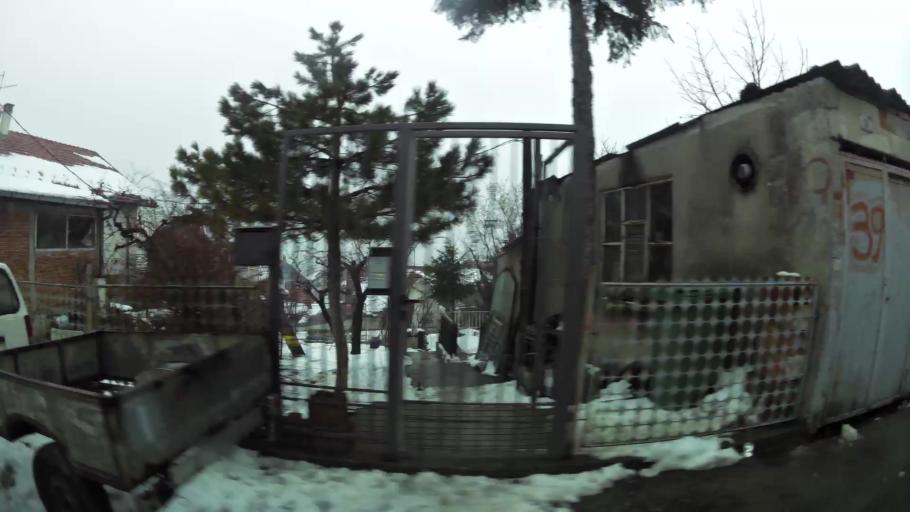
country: RS
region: Central Serbia
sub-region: Belgrade
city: Zvezdara
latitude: 44.7812
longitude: 20.5289
